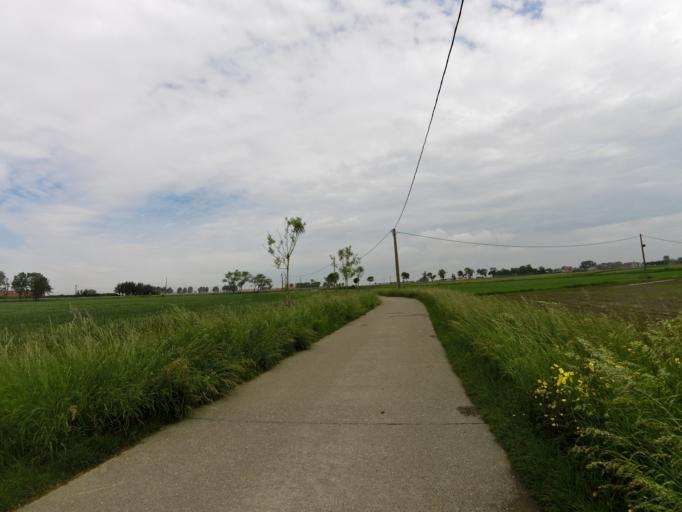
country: BE
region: Flanders
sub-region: Provincie West-Vlaanderen
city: Middelkerke
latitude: 51.1581
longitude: 2.8218
